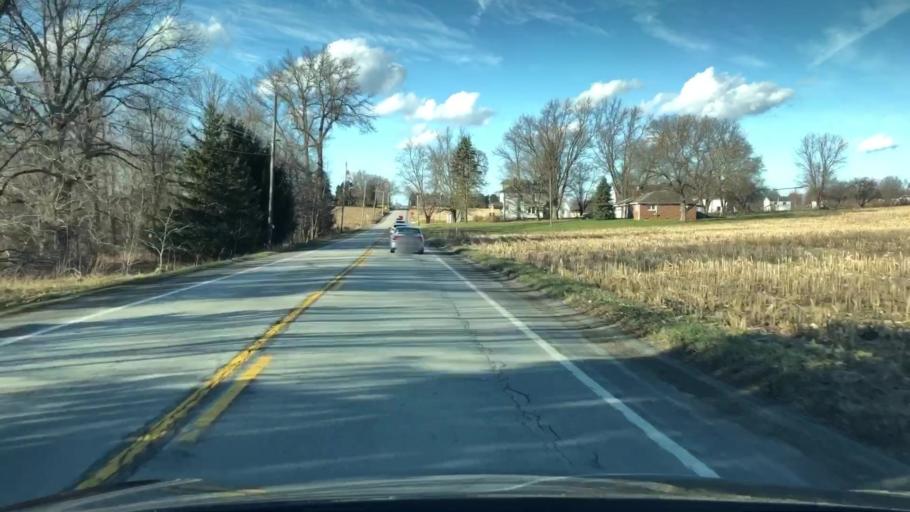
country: US
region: Pennsylvania
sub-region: Butler County
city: Saxonburg
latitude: 40.7513
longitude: -79.7733
